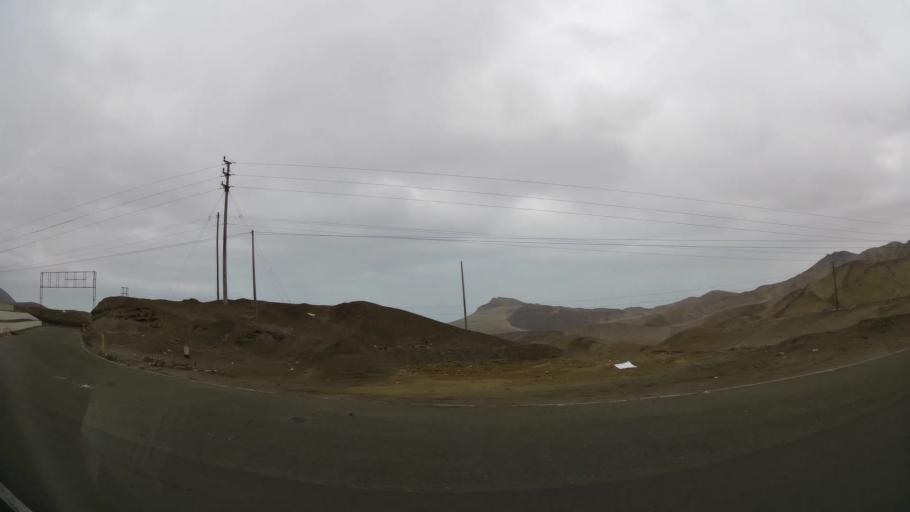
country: PE
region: Lima
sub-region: Lima
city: San Bartolo
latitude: -12.4345
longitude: -76.7546
